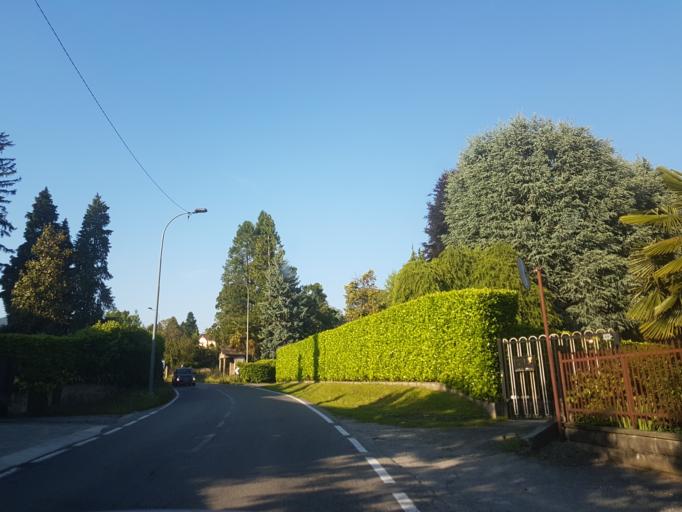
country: IT
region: Lombardy
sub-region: Provincia di Lecco
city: Oggiono
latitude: 45.7958
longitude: 9.3574
